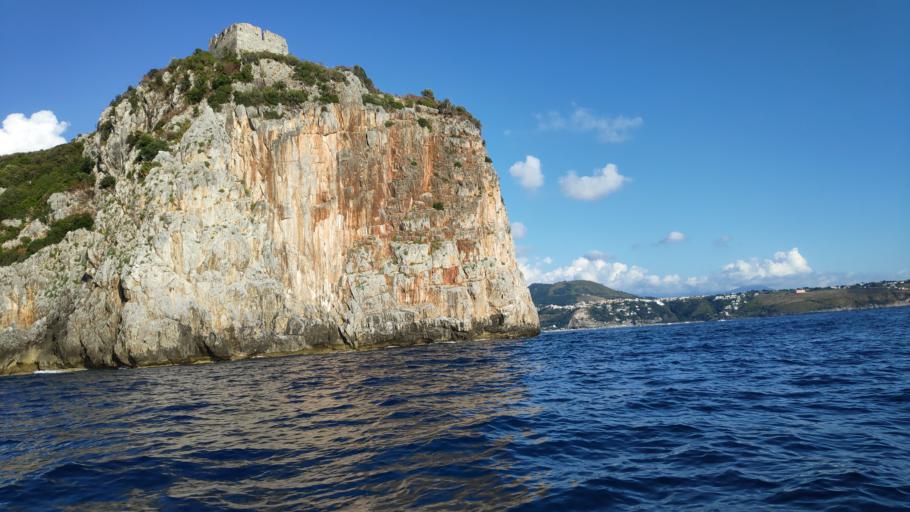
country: IT
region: Calabria
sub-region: Provincia di Cosenza
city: Praia a Mare
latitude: 39.8729
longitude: 15.7677
